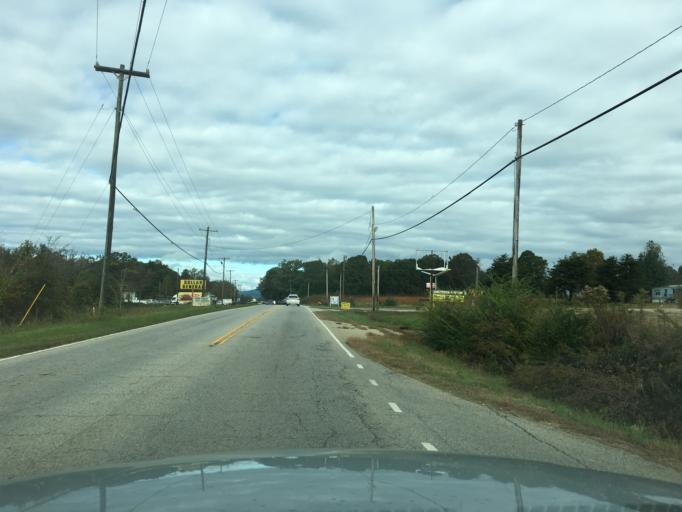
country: US
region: South Carolina
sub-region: Greenville County
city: Greer
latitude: 34.9946
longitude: -82.2469
